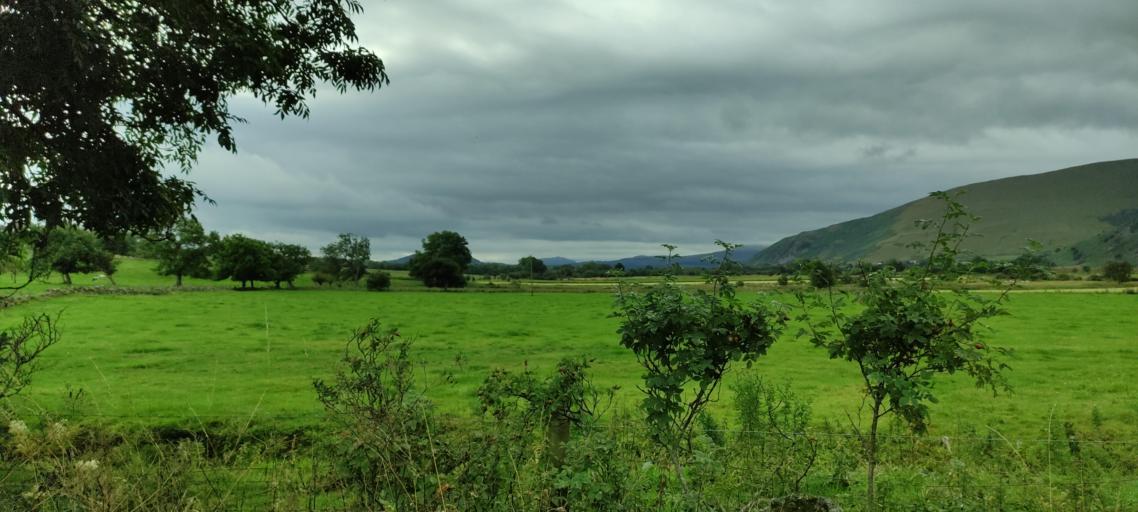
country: GB
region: England
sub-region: Cumbria
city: Keswick
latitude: 54.6995
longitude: -2.9914
